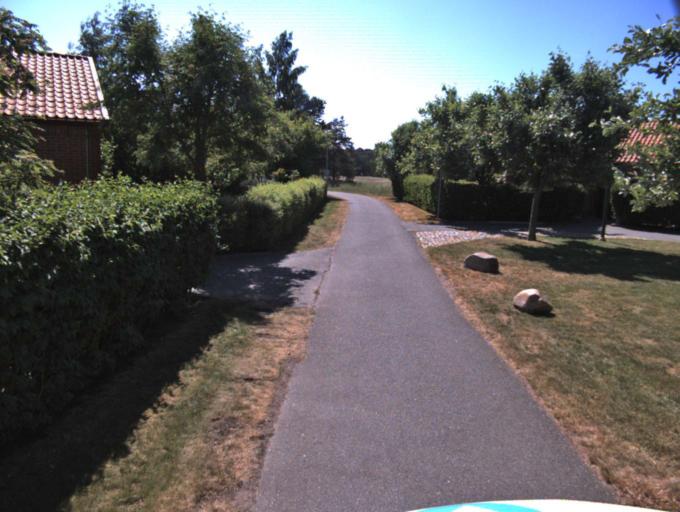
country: SE
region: Skane
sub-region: Kristianstads Kommun
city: Ahus
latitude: 55.9241
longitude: 14.2845
